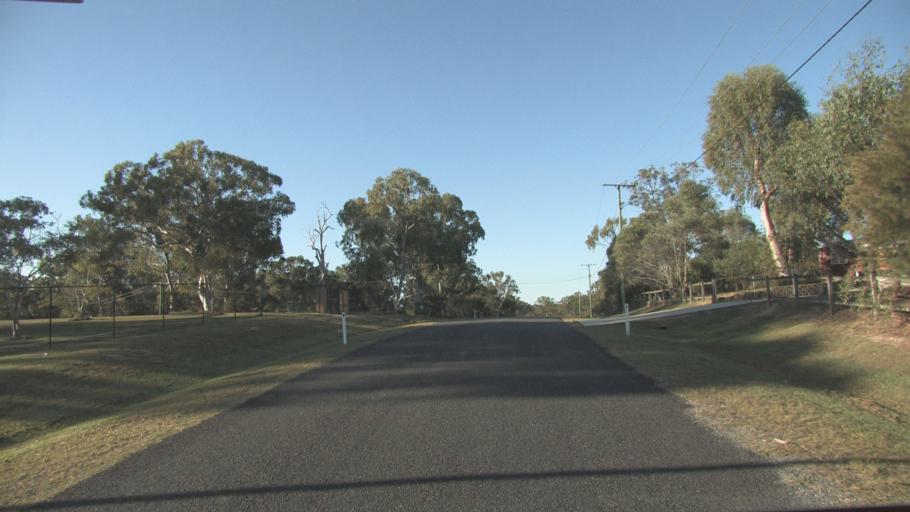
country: AU
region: Queensland
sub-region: Redland
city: Redland Bay
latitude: -27.6603
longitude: 153.2735
